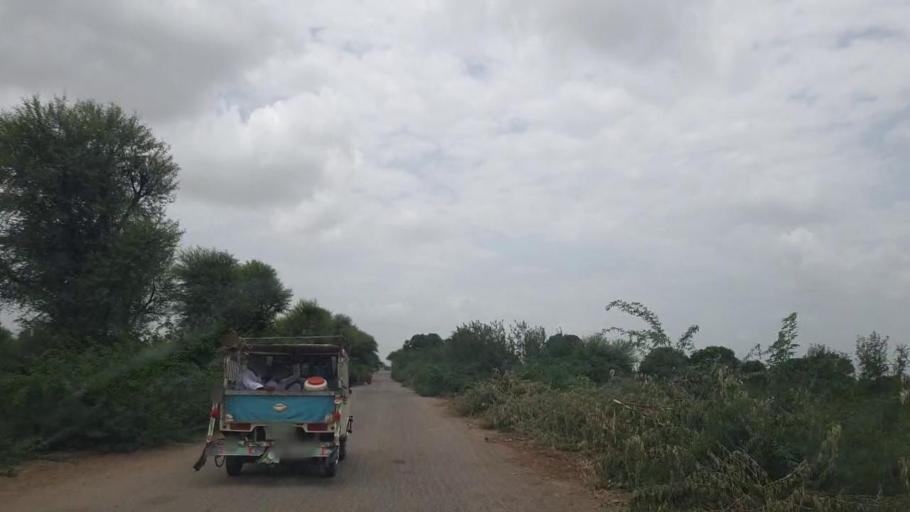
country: PK
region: Sindh
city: Naukot
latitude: 24.9035
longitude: 69.2621
